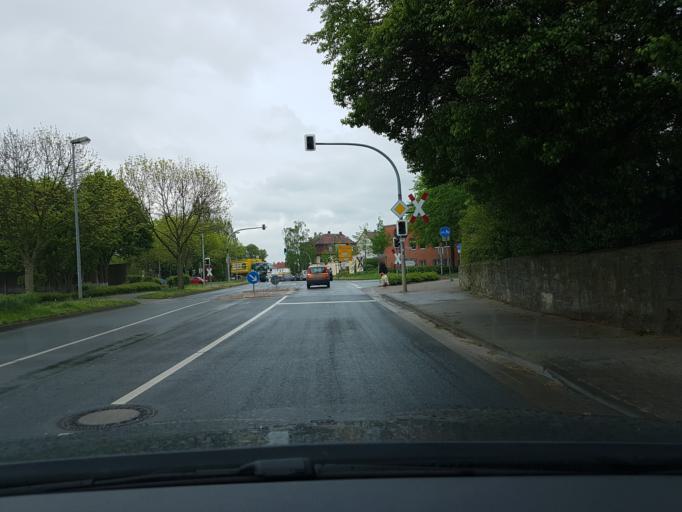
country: DE
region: Lower Saxony
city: Hameln
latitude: 52.0974
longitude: 9.3646
